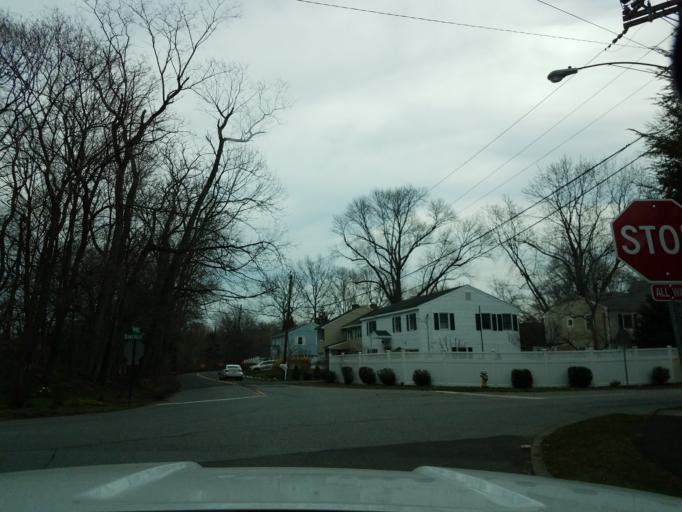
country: US
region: Connecticut
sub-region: Fairfield County
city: Riverside
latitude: 41.0377
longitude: -73.5649
